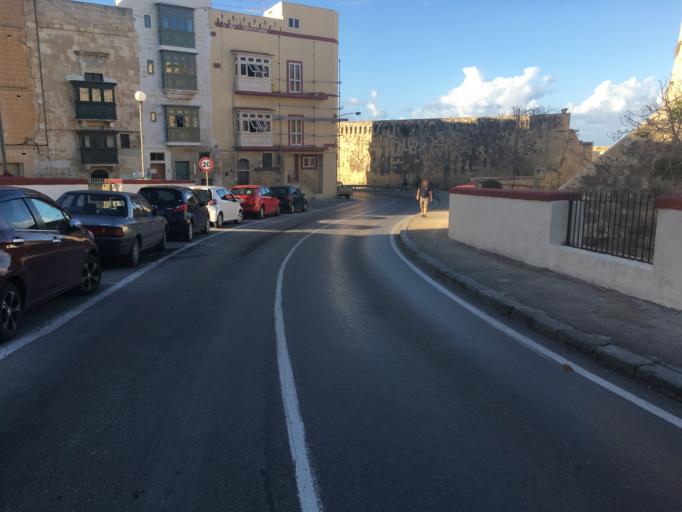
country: MT
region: Il-Belt Valletta
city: Valletta
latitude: 35.9012
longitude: 14.5178
